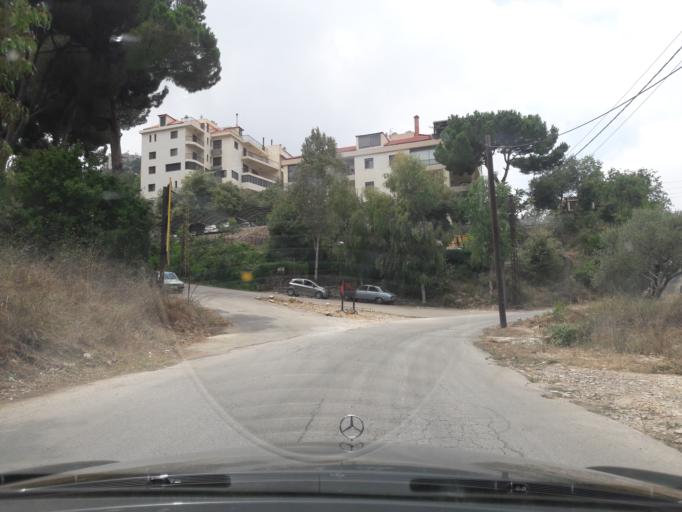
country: LB
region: Mont-Liban
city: Djounie
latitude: 33.9229
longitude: 35.6685
